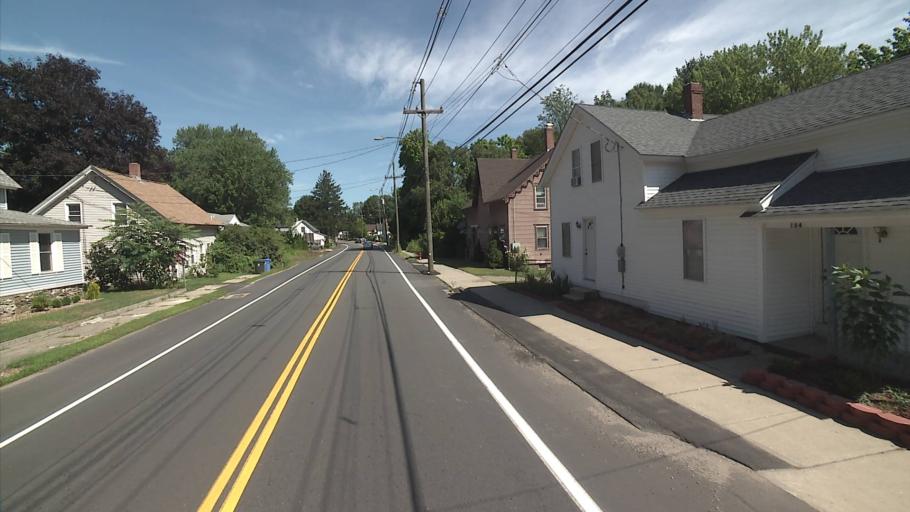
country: US
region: Connecticut
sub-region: New London County
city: Lisbon
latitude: 41.5894
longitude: -72.0478
